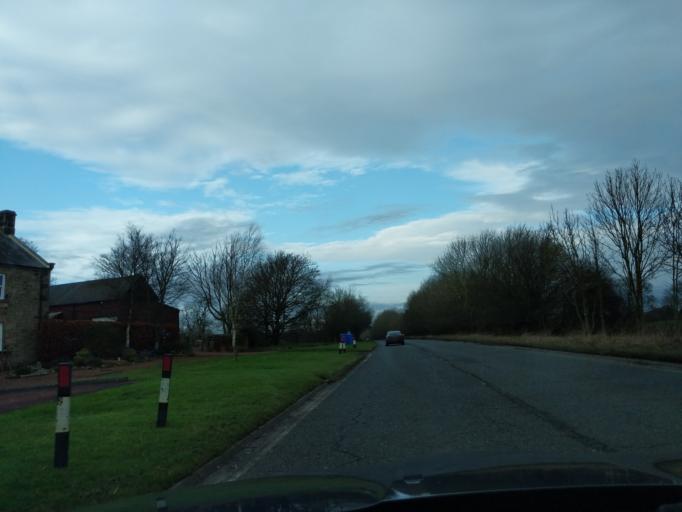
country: GB
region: England
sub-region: Northumberland
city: Meldon
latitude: 55.0887
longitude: -1.8113
